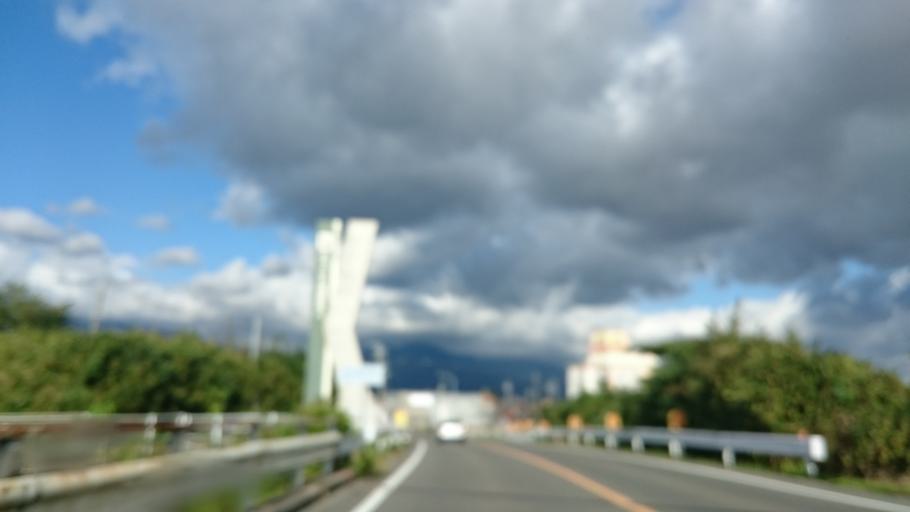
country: JP
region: Mie
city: Komono
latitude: 34.9995
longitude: 136.5402
